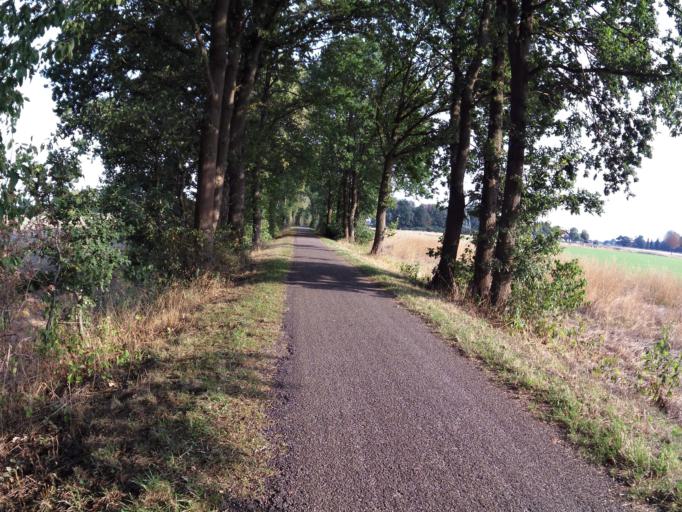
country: DE
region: North Rhine-Westphalia
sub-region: Regierungsbezirk Detmold
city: Petershagen
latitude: 52.3994
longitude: 8.9637
